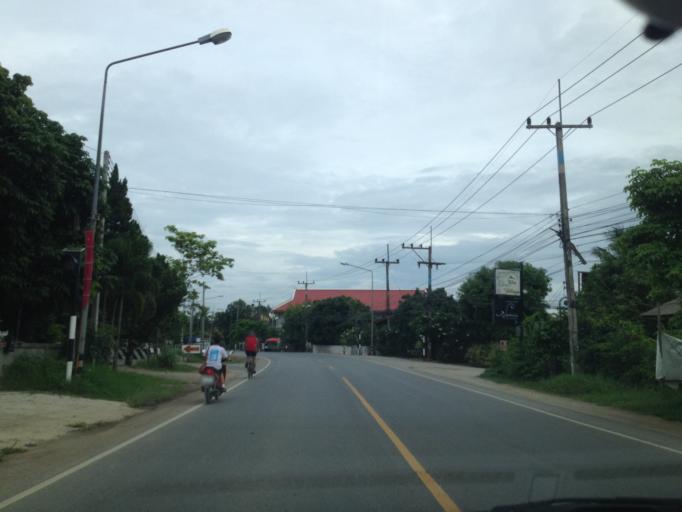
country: TH
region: Chiang Mai
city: Hang Dong
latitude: 18.7303
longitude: 98.9073
